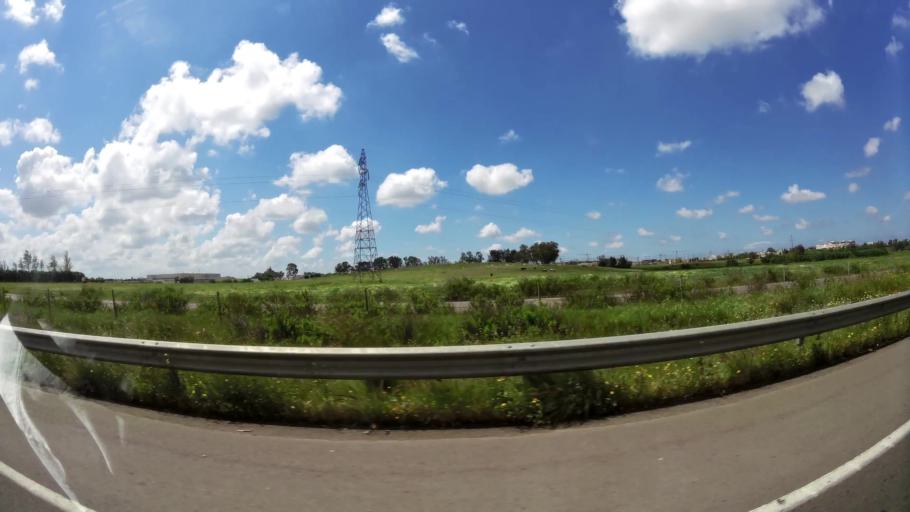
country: MA
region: Grand Casablanca
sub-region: Nouaceur
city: Bouskoura
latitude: 33.4595
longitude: -7.6335
